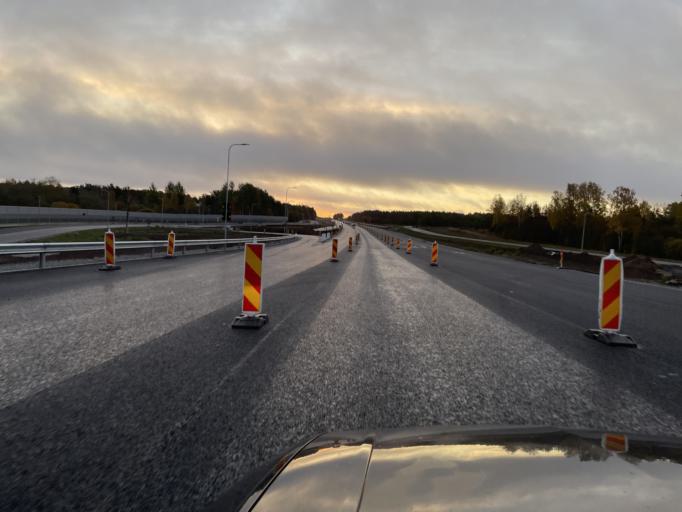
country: EE
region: Harju
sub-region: Saue linn
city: Saue
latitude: 59.3155
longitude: 24.5249
